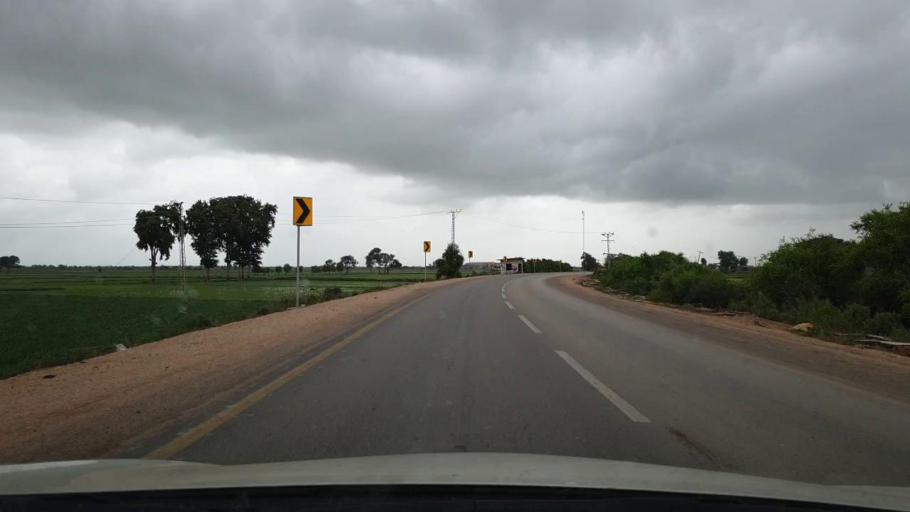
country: PK
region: Sindh
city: Kario
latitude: 24.6518
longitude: 68.4988
